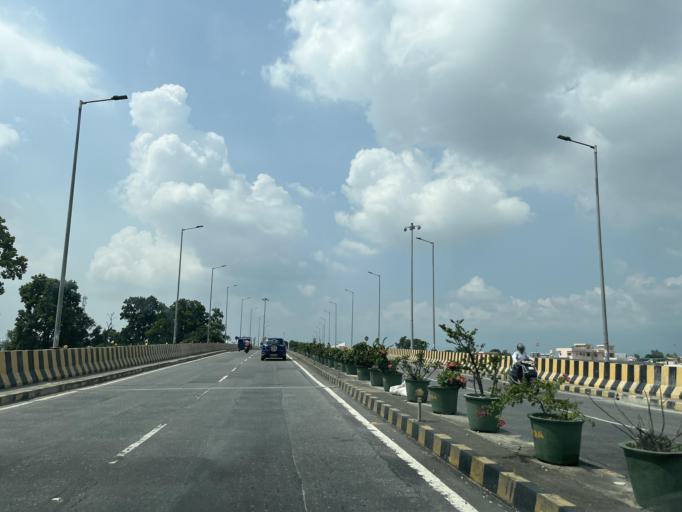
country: IN
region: Uttarakhand
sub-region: Dehradun
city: Raipur
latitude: 30.2765
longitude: 78.0749
